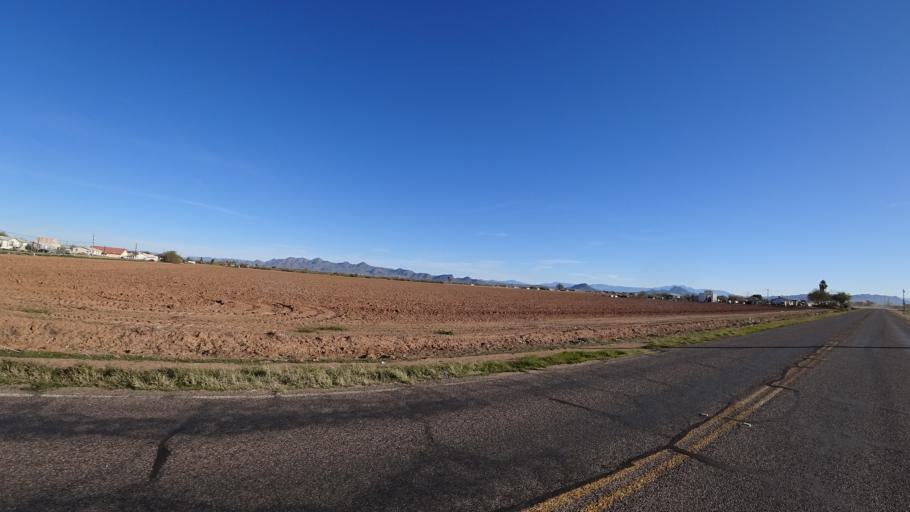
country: US
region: Arizona
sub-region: Maricopa County
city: Scottsdale
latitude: 33.4806
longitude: -111.8476
